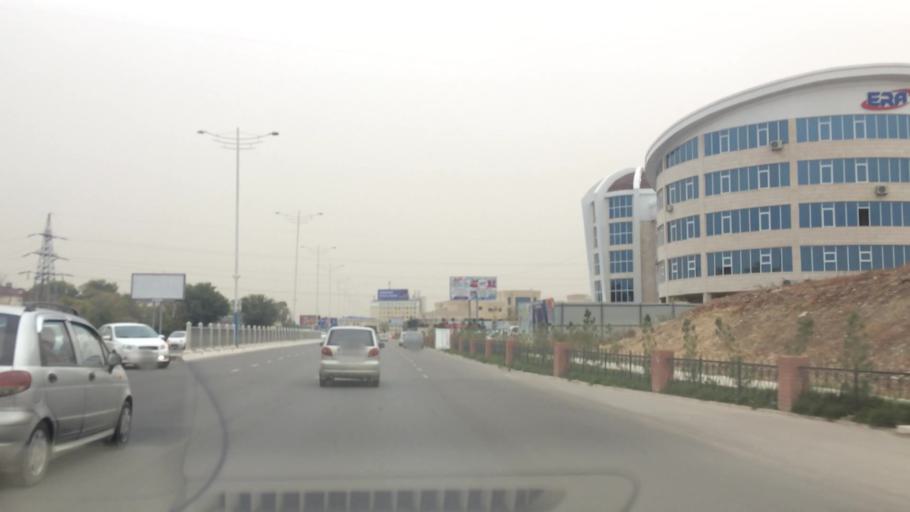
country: UZ
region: Toshkent Shahri
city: Bektemir
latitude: 41.3043
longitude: 69.3120
